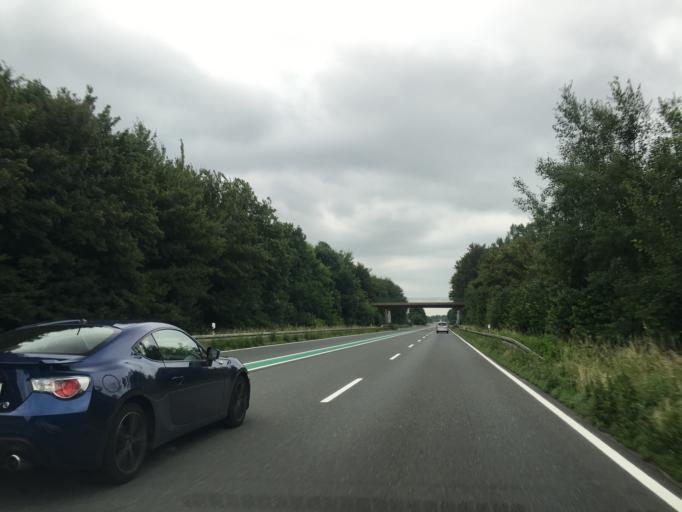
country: DE
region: North Rhine-Westphalia
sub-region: Regierungsbezirk Munster
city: Altenberge
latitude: 52.0597
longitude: 7.4388
